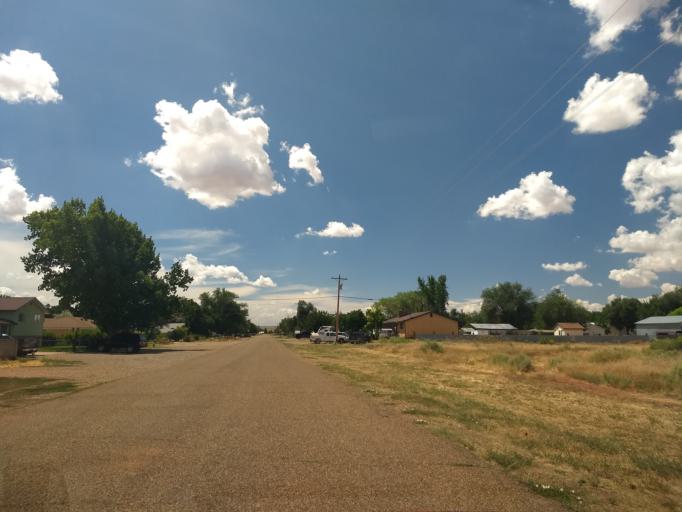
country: US
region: Arizona
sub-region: Coconino County
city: Fredonia
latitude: 36.9524
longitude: -112.5243
